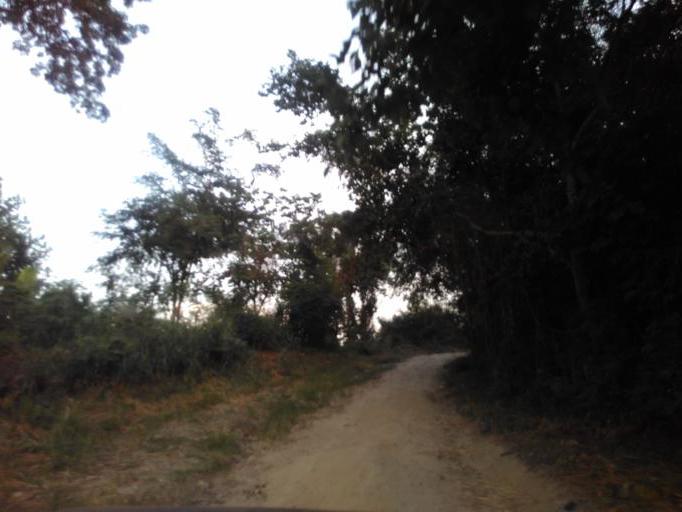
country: GH
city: Bekwai
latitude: 6.5340
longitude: -1.4317
